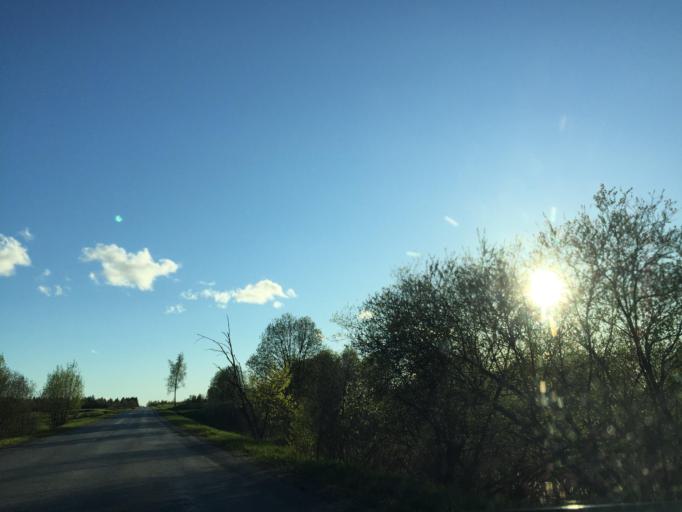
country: LV
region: Ergli
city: Ergli
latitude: 56.8735
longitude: 25.8173
